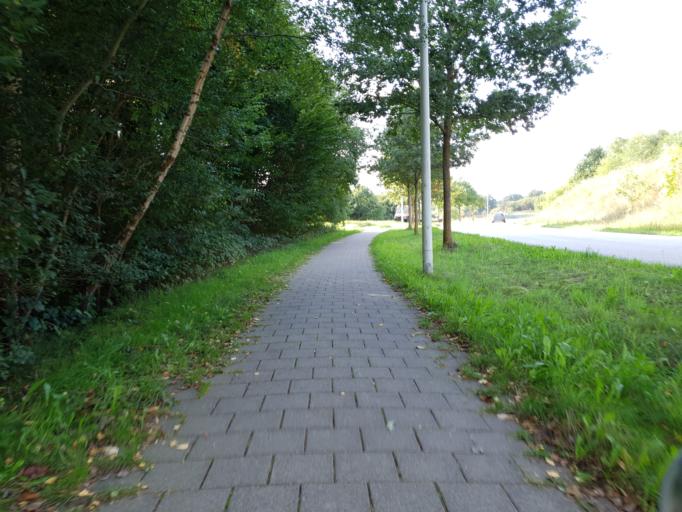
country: DE
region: Schleswig-Holstein
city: Kronshagen
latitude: 54.3483
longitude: 10.0765
